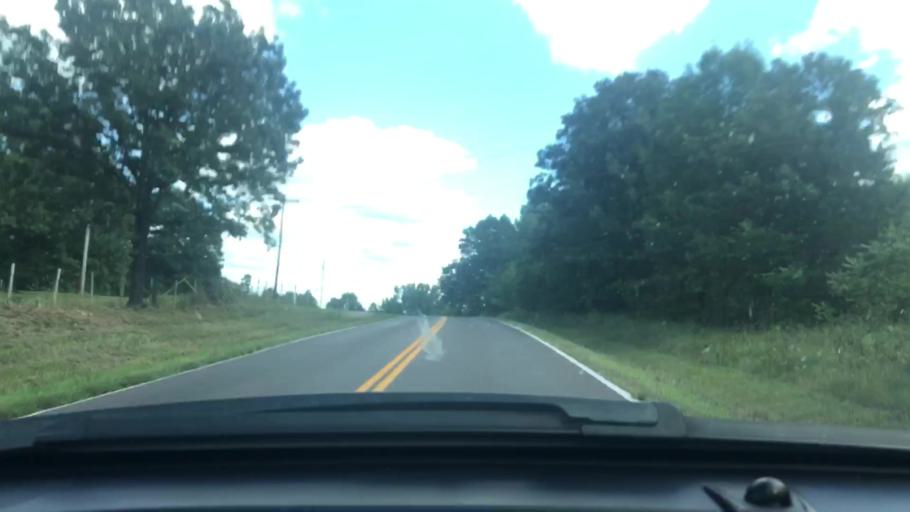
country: US
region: Missouri
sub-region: Wright County
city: Hartville
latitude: 37.3527
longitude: -92.3389
